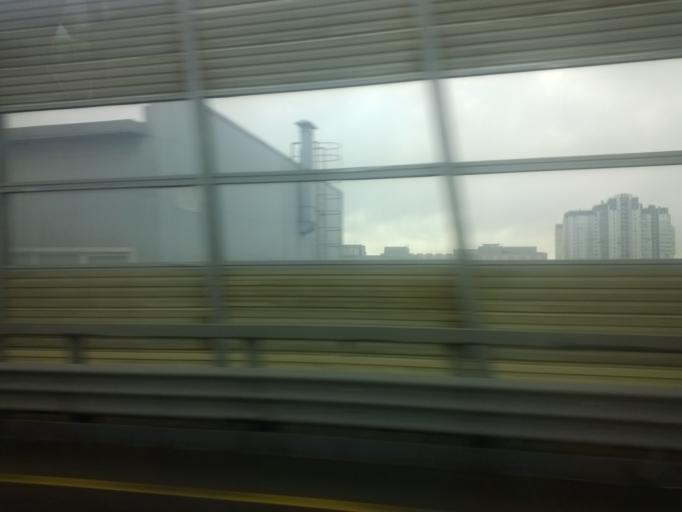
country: RU
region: St.-Petersburg
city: Avtovo
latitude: 59.8555
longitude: 30.2839
